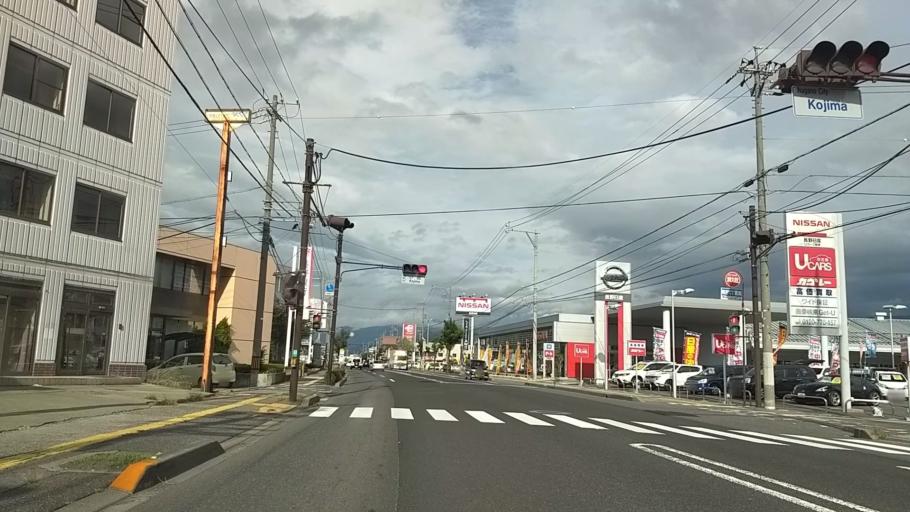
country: JP
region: Nagano
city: Suzaka
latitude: 36.6576
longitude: 138.2514
